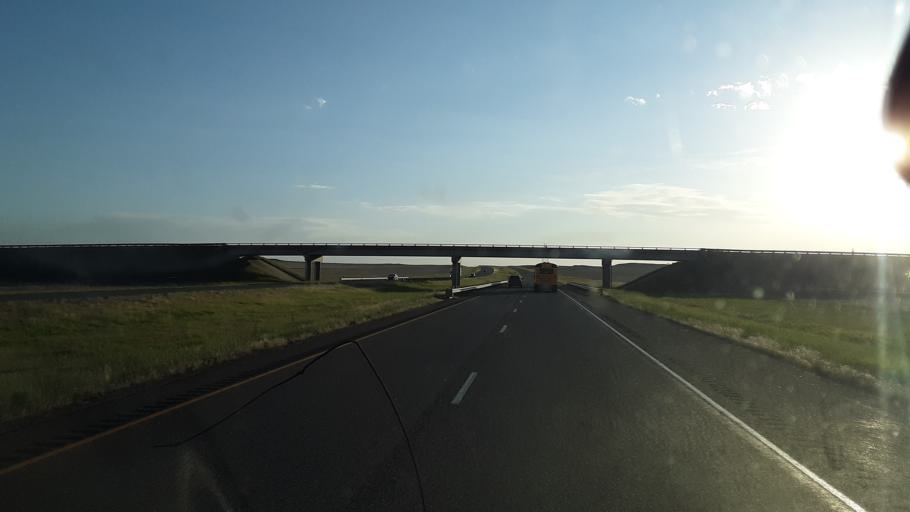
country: US
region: Montana
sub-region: Big Horn County
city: Hardin
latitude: 45.7463
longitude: -107.6807
